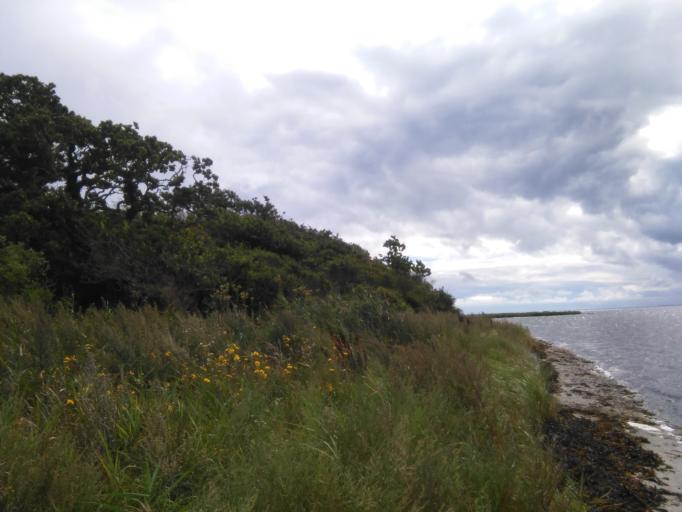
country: DK
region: Central Jutland
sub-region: Odder Kommune
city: Odder
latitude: 55.8602
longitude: 10.1394
